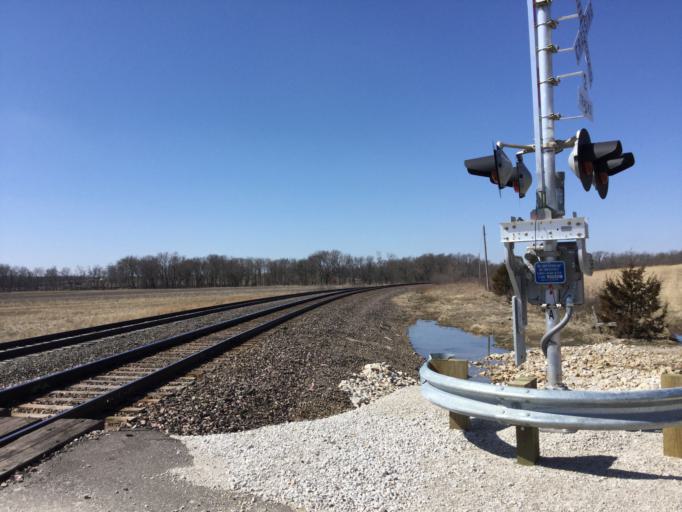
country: US
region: Kansas
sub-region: Anderson County
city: Garnett
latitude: 38.1911
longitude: -95.4625
